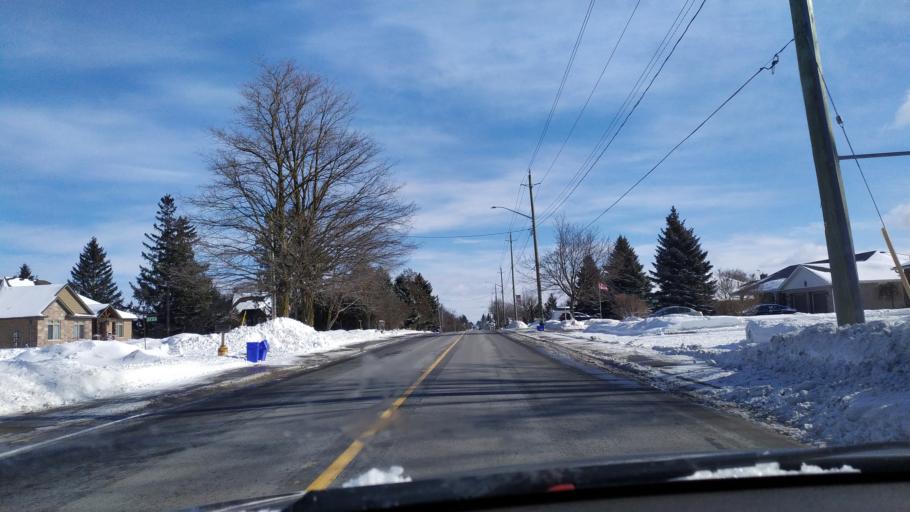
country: CA
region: Ontario
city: Waterloo
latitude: 43.5237
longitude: -80.6598
